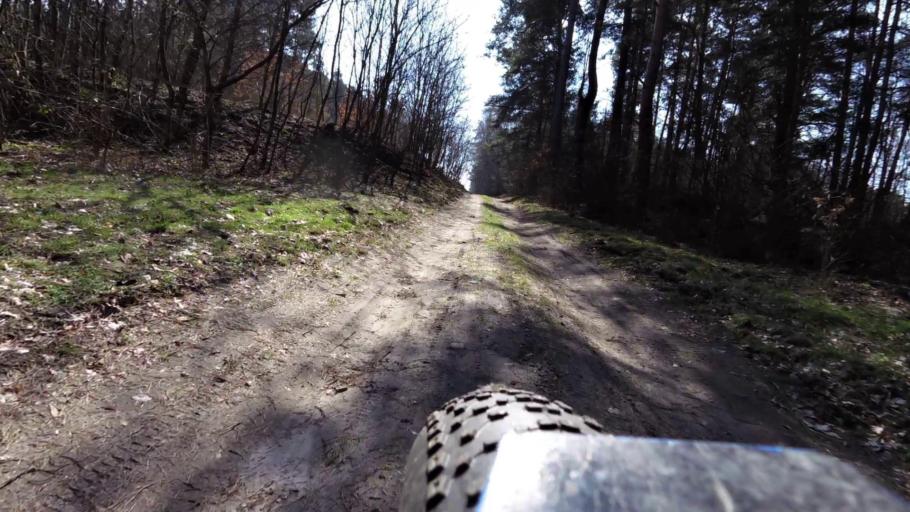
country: PL
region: Lubusz
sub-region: Powiat slubicki
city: Cybinka
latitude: 52.2064
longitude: 14.8999
